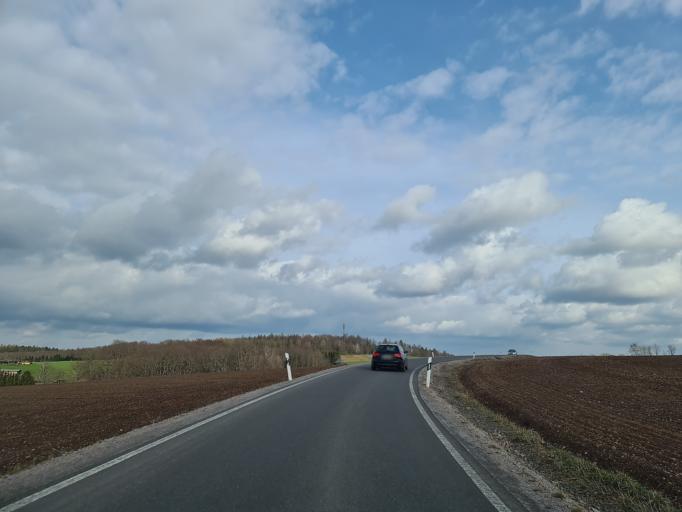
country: DE
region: Saxony
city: Lichtenstein
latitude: 50.7169
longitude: 12.6282
